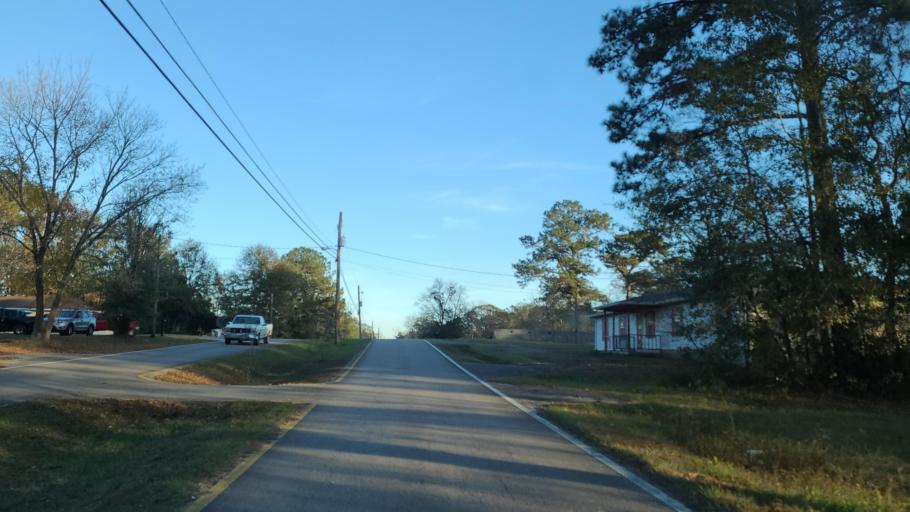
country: US
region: Mississippi
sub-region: Lamar County
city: Lumberton
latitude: 31.0060
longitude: -89.4648
